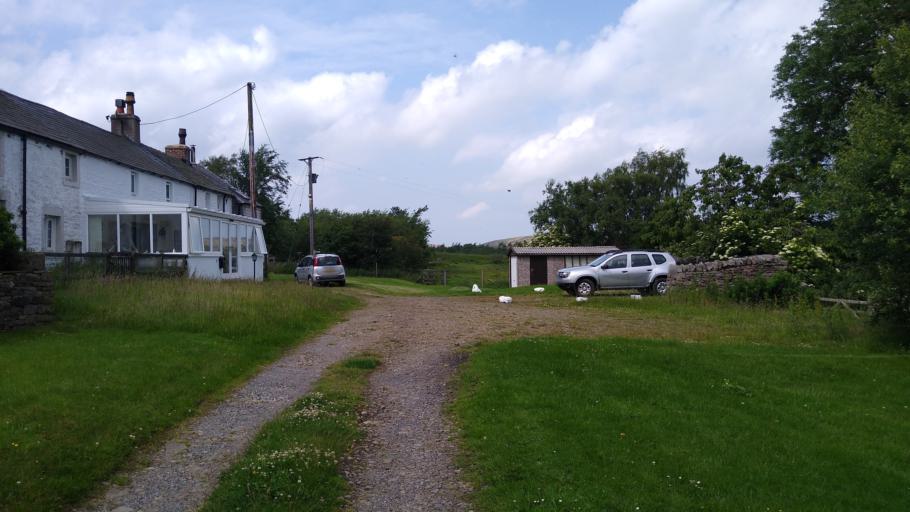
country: GB
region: England
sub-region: Cumbria
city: Brampton
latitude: 54.9094
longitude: -2.6381
